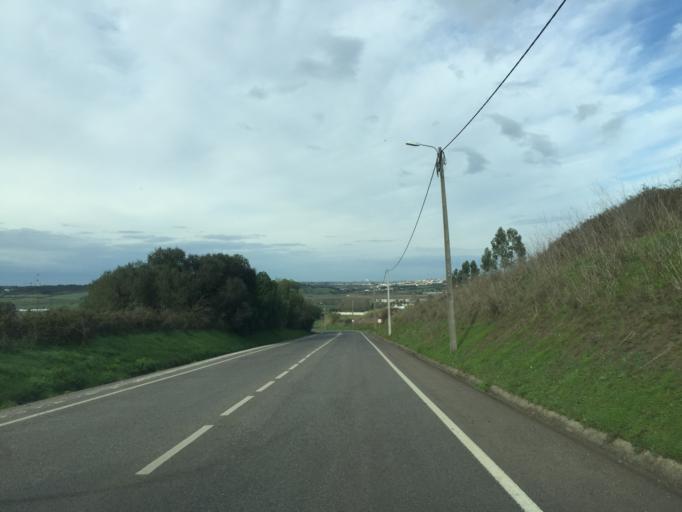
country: PT
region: Lisbon
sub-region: Sintra
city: Almargem
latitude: 38.8522
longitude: -9.2693
